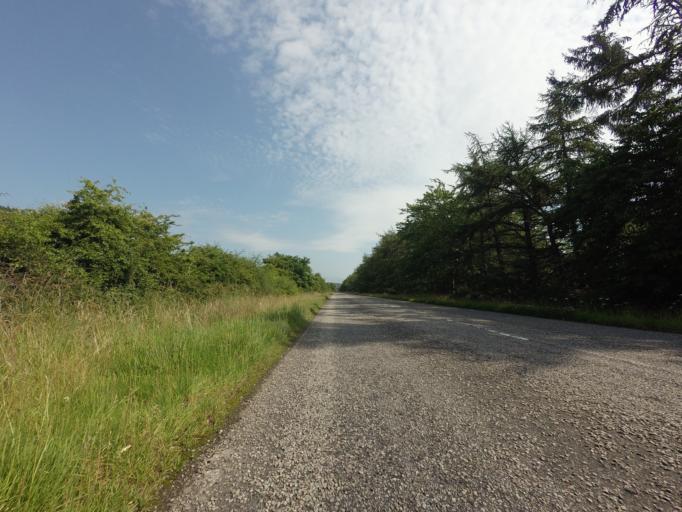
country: GB
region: Scotland
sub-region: Highland
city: Evanton
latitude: 57.9170
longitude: -4.3919
